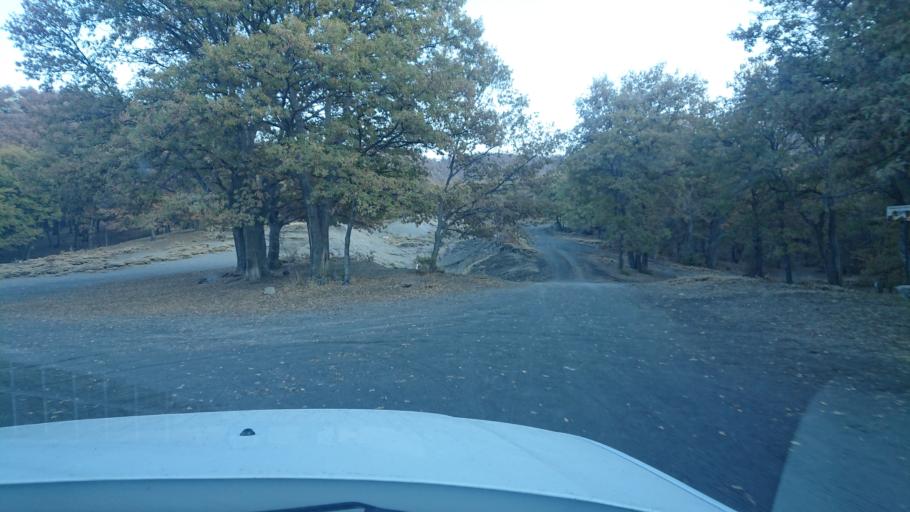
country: TR
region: Aksaray
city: Taspinar
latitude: 38.1660
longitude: 34.2052
